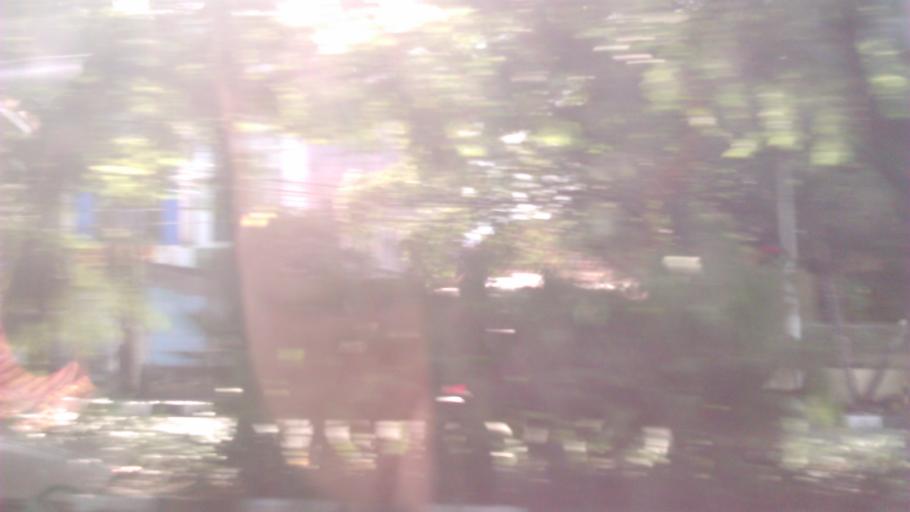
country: ID
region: East Java
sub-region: Kota Surabaya
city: Surabaya
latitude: -7.2558
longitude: 112.7503
